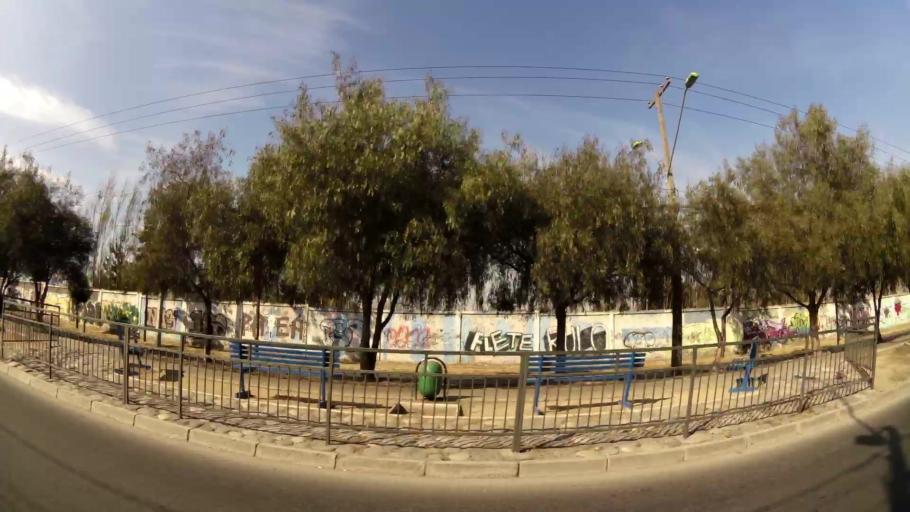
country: CL
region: Santiago Metropolitan
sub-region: Provincia de Santiago
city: La Pintana
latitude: -33.5655
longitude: -70.6321
